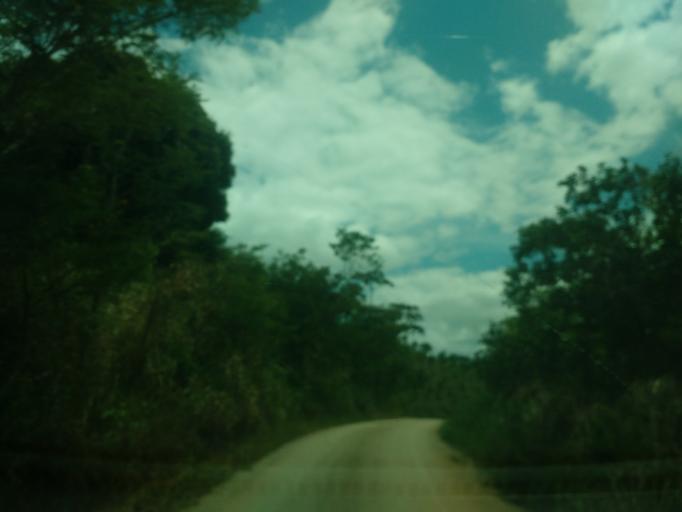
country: BR
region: Alagoas
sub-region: Santana Do Mundau
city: Santana do Mundau
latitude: -9.1571
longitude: -36.1605
